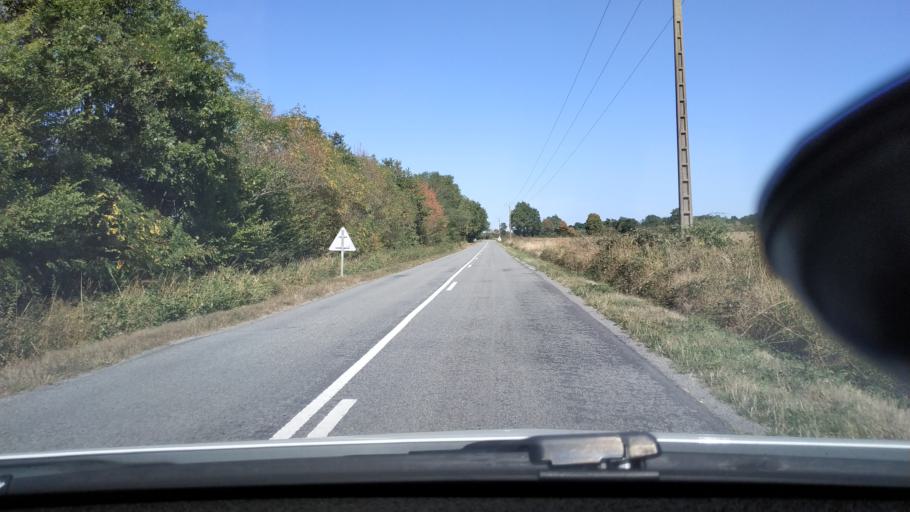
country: FR
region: Centre
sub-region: Departement du Loiret
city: Coullons
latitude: 47.6316
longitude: 2.5117
